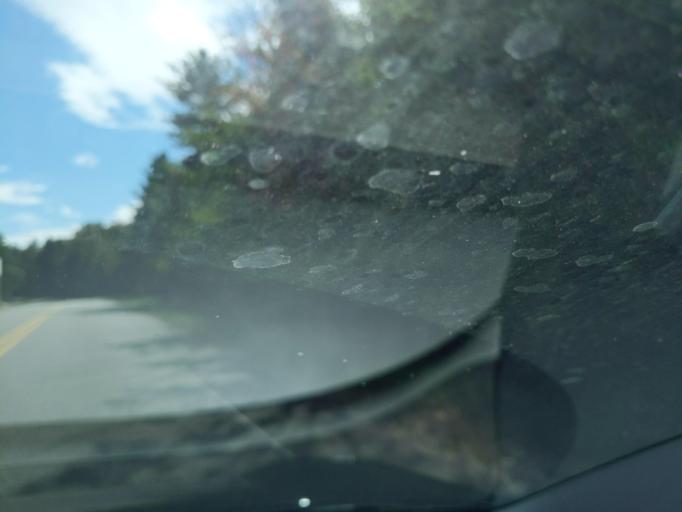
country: US
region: Michigan
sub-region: Antrim County
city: Bellaire
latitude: 45.0590
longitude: -85.3188
